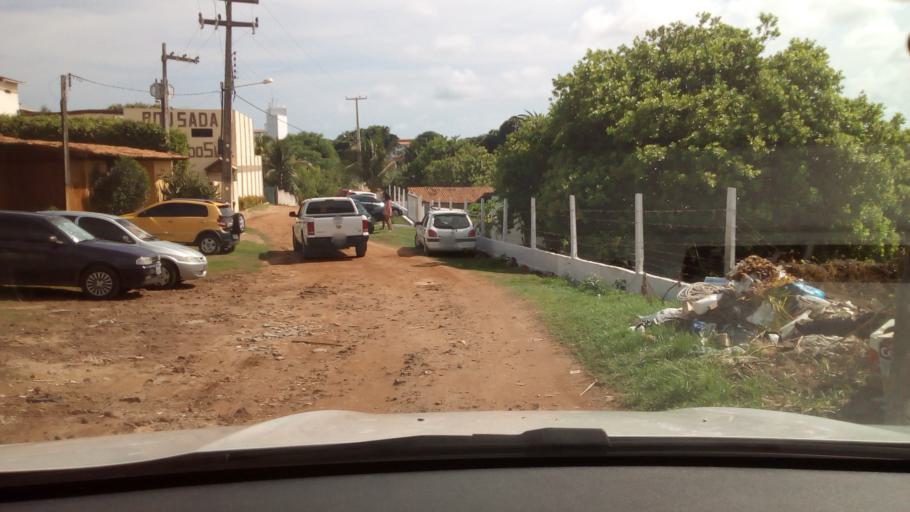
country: BR
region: Paraiba
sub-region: Conde
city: Conde
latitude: -7.3005
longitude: -34.8001
